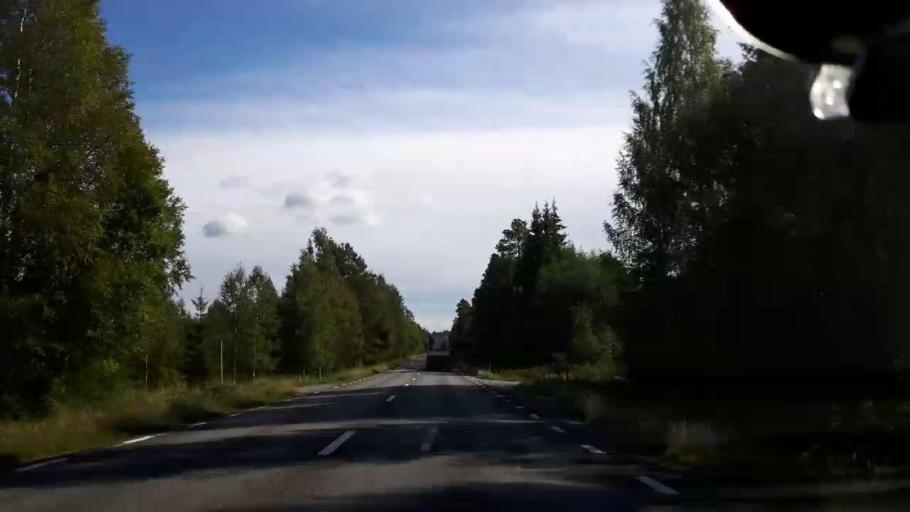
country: SE
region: Jaemtland
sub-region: Braecke Kommun
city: Braecke
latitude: 63.1885
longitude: 15.4787
